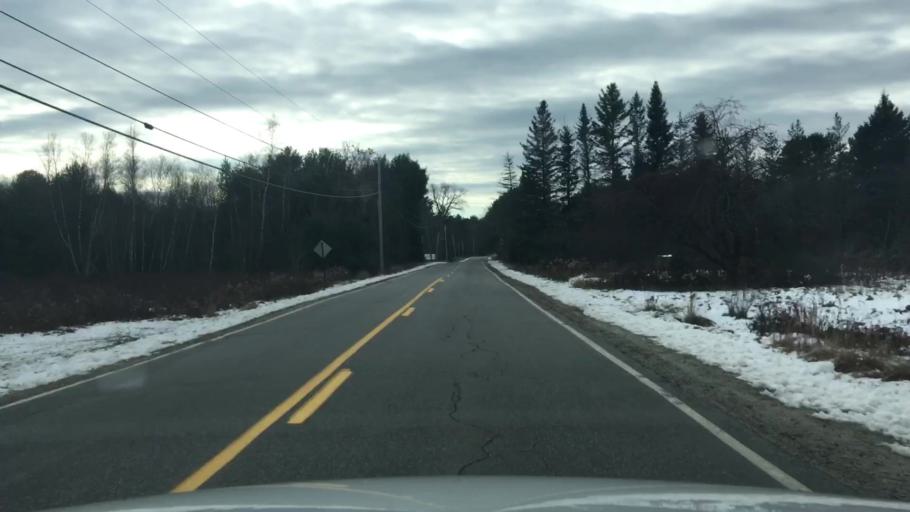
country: US
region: Maine
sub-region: Oxford County
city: Canton
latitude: 44.4529
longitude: -70.3035
